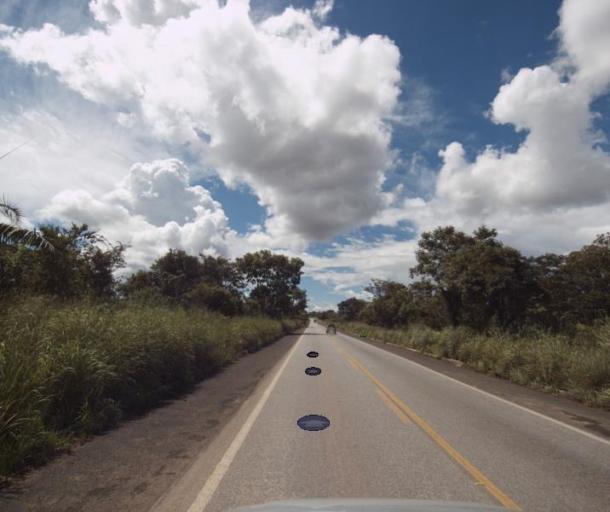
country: BR
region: Goias
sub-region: Uruacu
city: Uruacu
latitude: -14.0638
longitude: -49.0934
